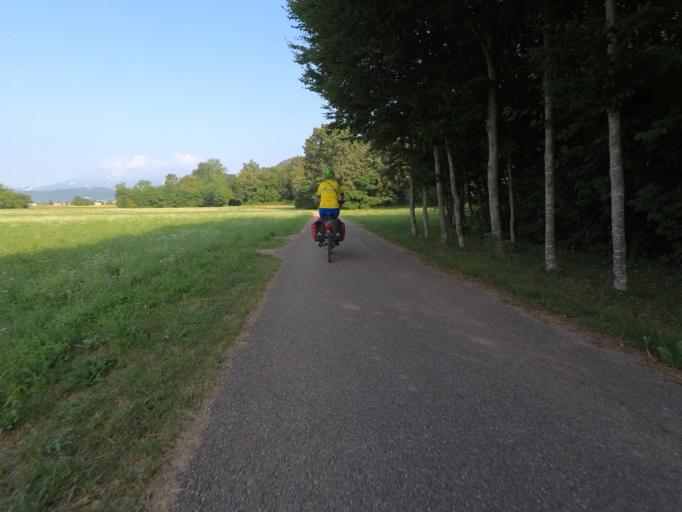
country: IT
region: Friuli Venezia Giulia
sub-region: Provincia di Pordenone
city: Travesio
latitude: 46.1998
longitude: 12.8494
